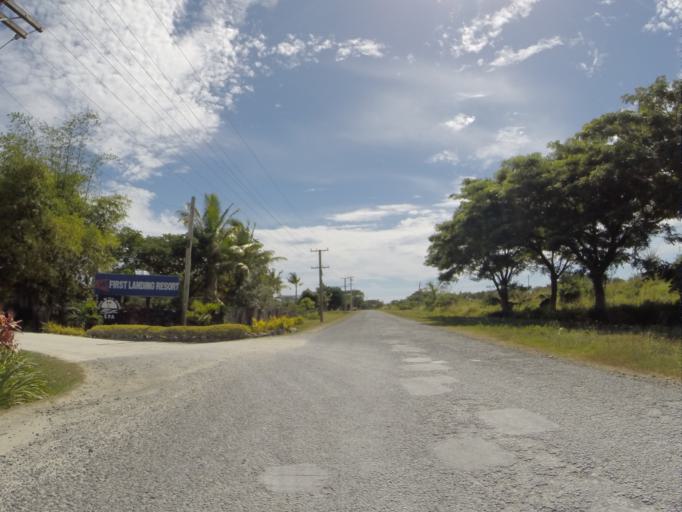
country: FJ
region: Western
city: Lautoka
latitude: -17.6786
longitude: 177.3867
